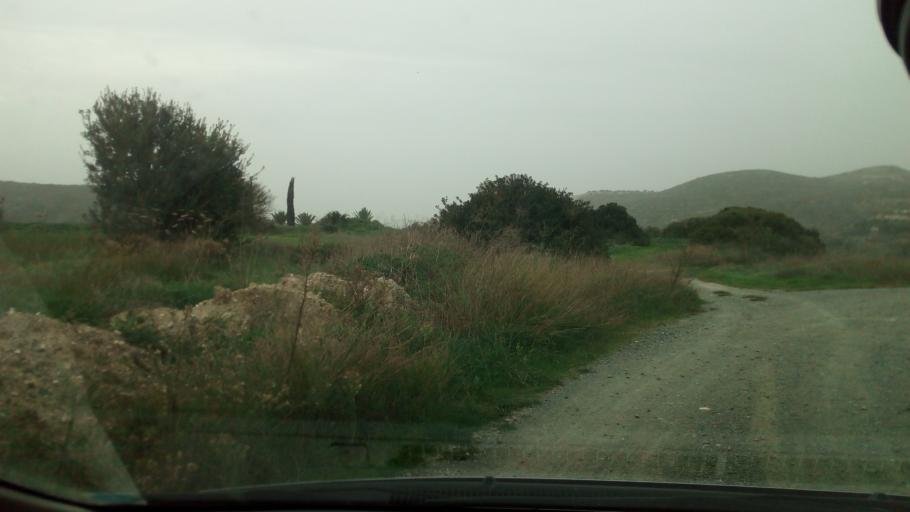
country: CY
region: Limassol
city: Pyrgos
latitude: 34.7212
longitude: 33.2349
